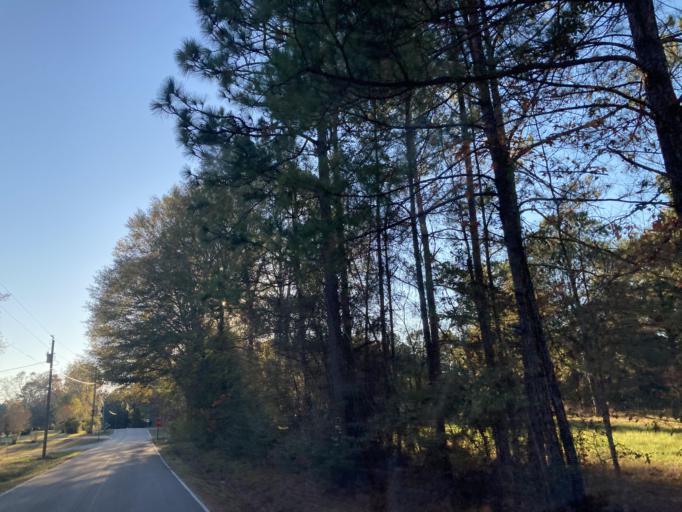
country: US
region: Mississippi
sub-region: Marion County
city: Columbia
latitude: 31.2388
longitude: -89.6376
